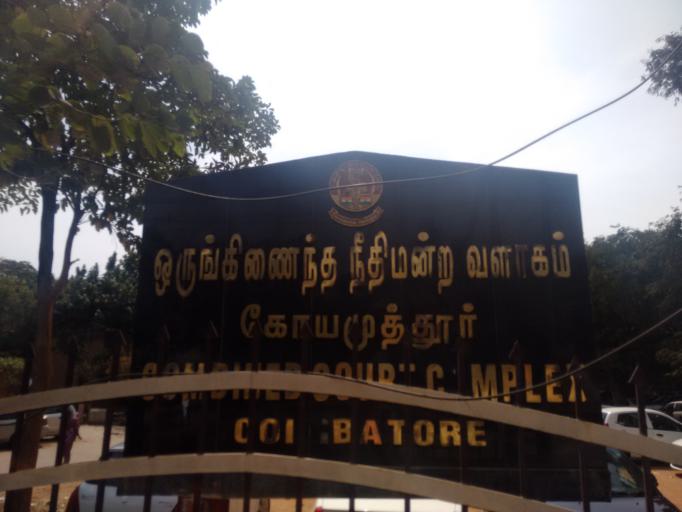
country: IN
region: Tamil Nadu
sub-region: Coimbatore
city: Coimbatore
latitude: 11.0007
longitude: 76.9698
